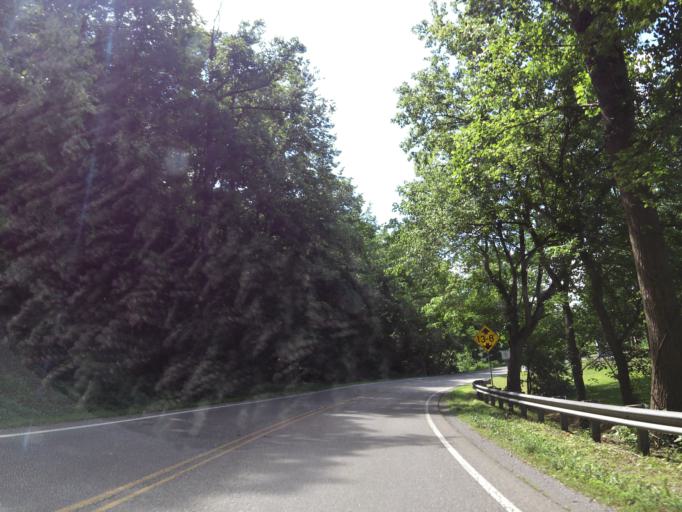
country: US
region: Virginia
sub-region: Lee County
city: Pennington Gap
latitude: 36.7575
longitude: -83.0121
